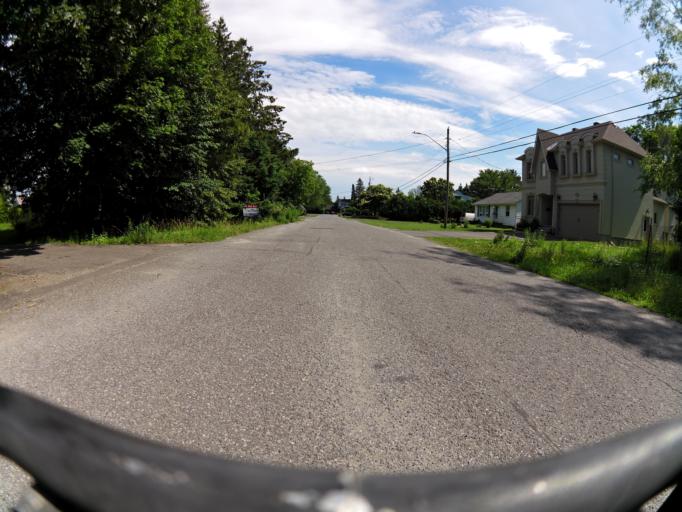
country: CA
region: Ontario
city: Ottawa
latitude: 45.3550
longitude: -75.7163
